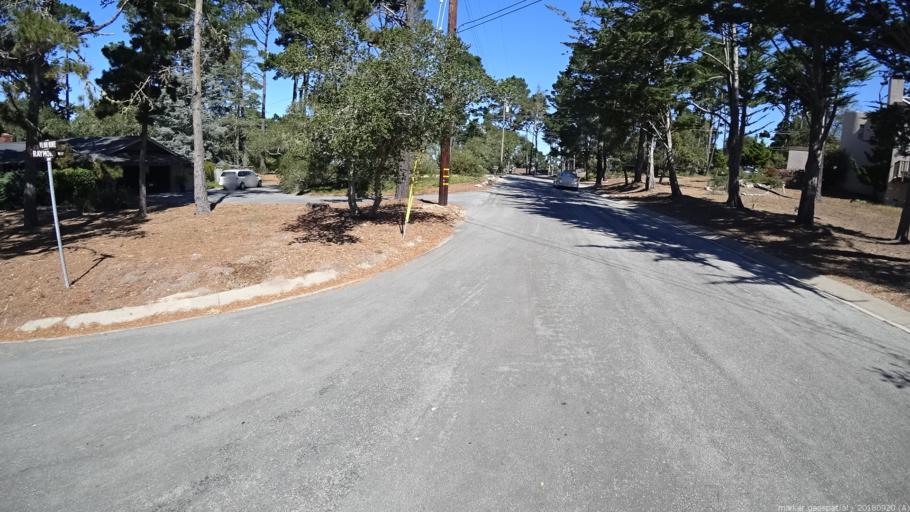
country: US
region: California
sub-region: Monterey County
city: Carmel-by-the-Sea
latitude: 36.5696
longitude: -121.9077
